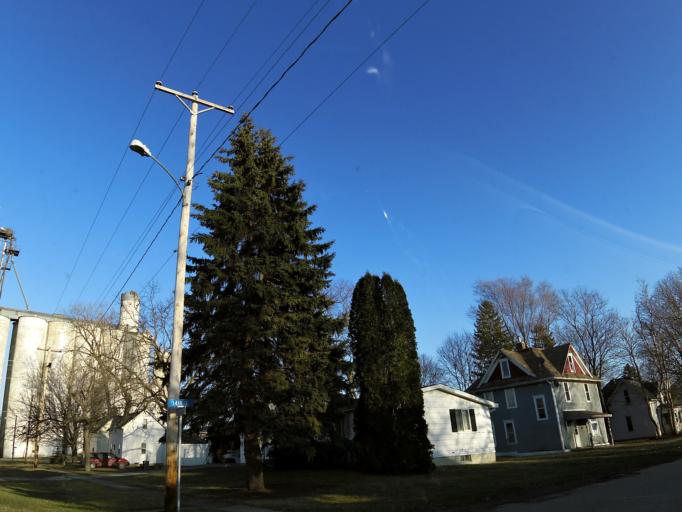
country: US
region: Iowa
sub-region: Worth County
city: Northwood
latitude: 43.4451
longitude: -93.2134
